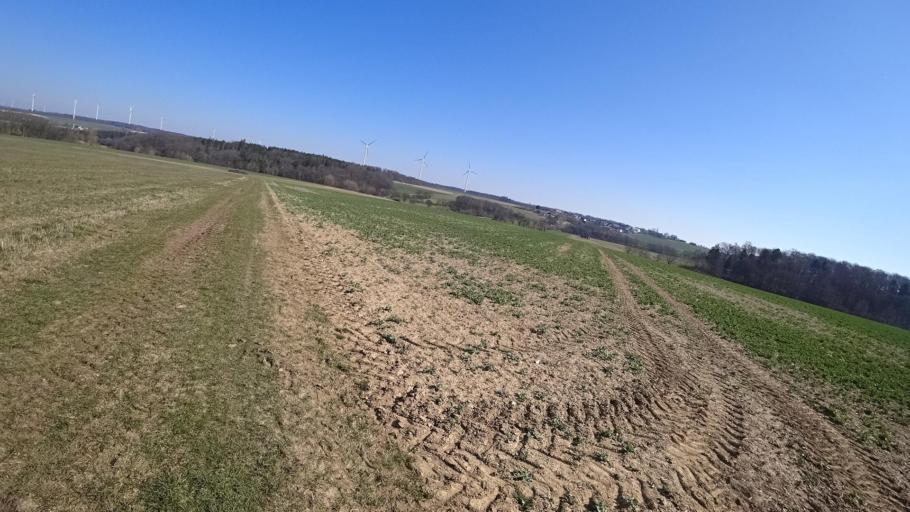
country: DE
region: Rheinland-Pfalz
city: Rayerschied
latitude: 50.0003
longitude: 7.5791
